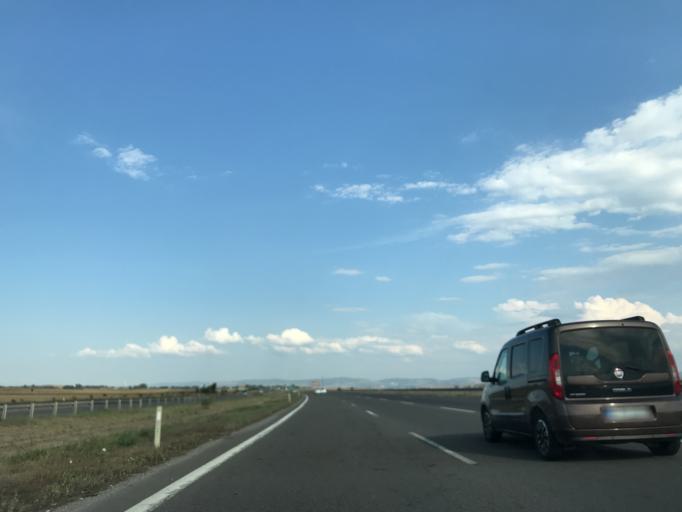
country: TR
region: Bolu
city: Dortdivan
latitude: 40.7475
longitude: 32.0907
